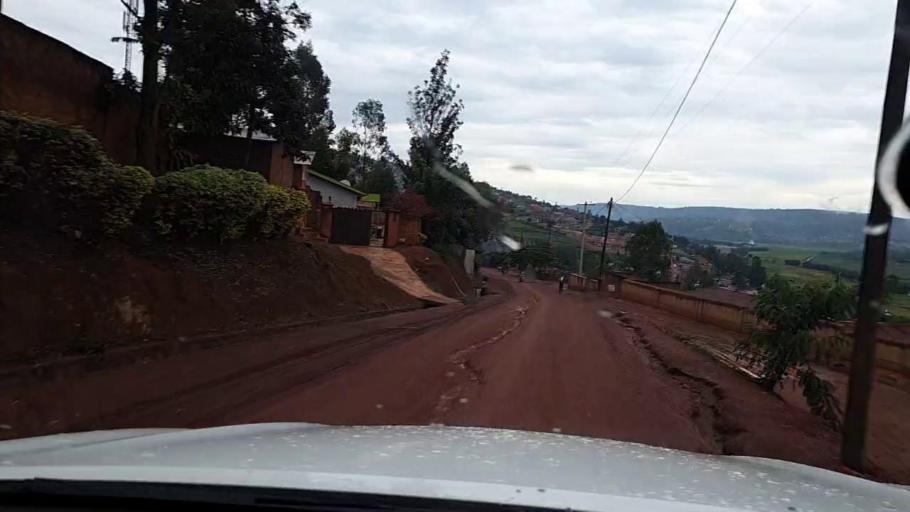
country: RW
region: Kigali
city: Kigali
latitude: -1.9065
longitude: 30.0477
